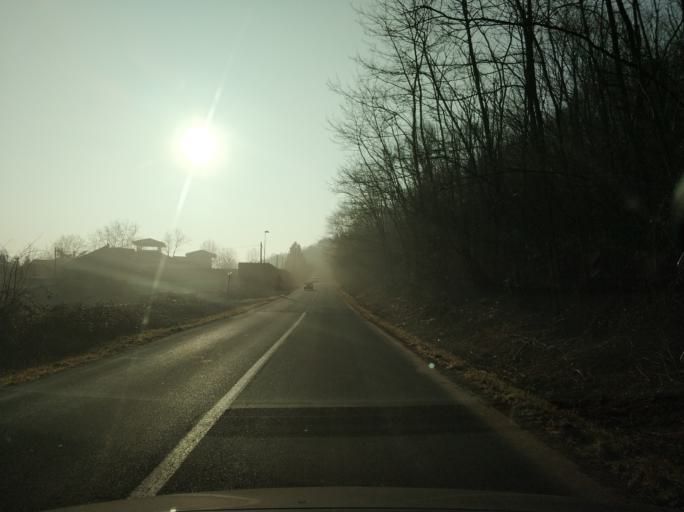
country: IT
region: Piedmont
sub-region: Provincia di Torino
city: Rivarossa
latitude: 45.2581
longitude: 7.7027
